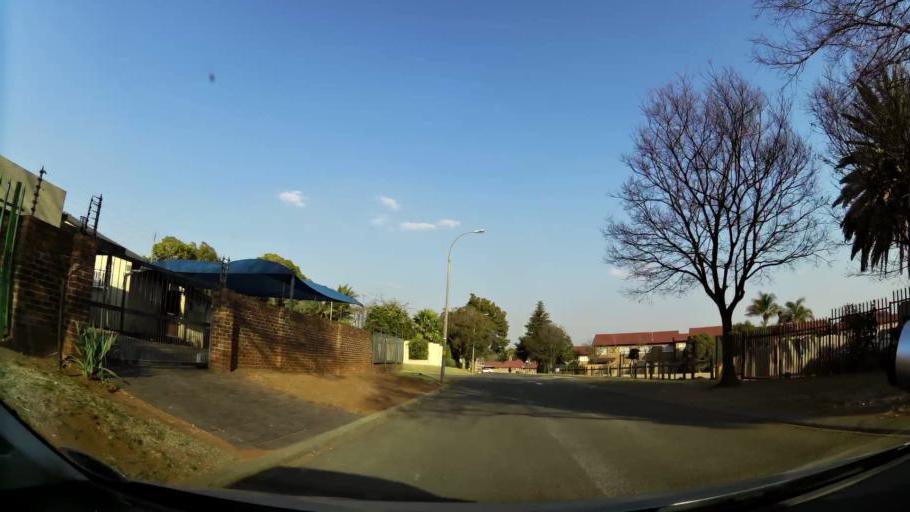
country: ZA
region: Gauteng
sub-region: City of Johannesburg Metropolitan Municipality
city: Modderfontein
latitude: -26.0688
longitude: 28.2220
